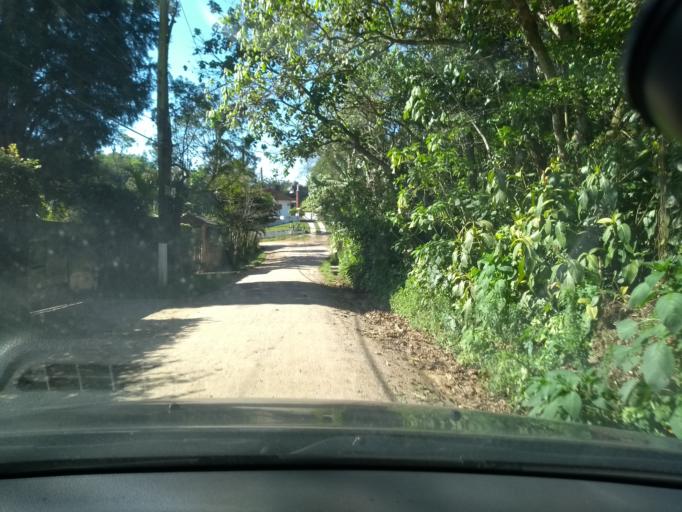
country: BR
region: Sao Paulo
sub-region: Rio Grande Da Serra
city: Rio Grande da Serra
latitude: -23.7601
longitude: -46.4739
